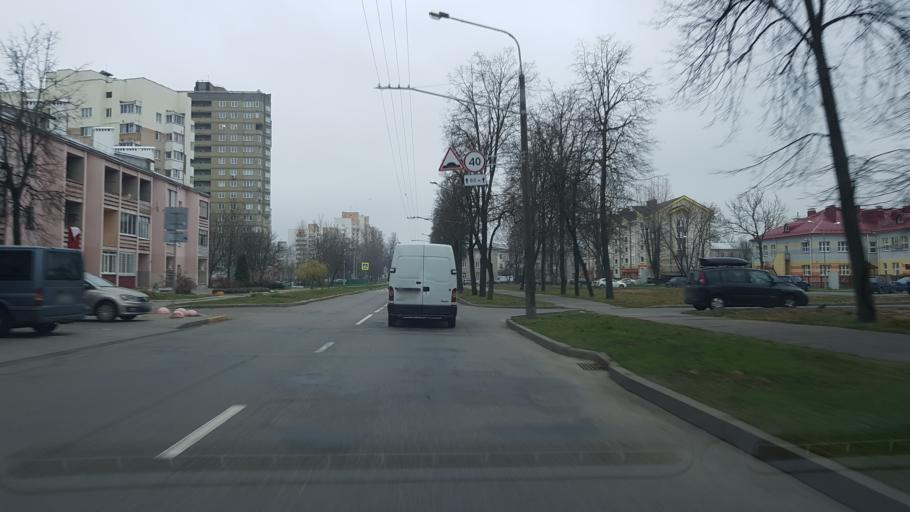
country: BY
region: Minsk
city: Minsk
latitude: 53.9293
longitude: 27.5415
